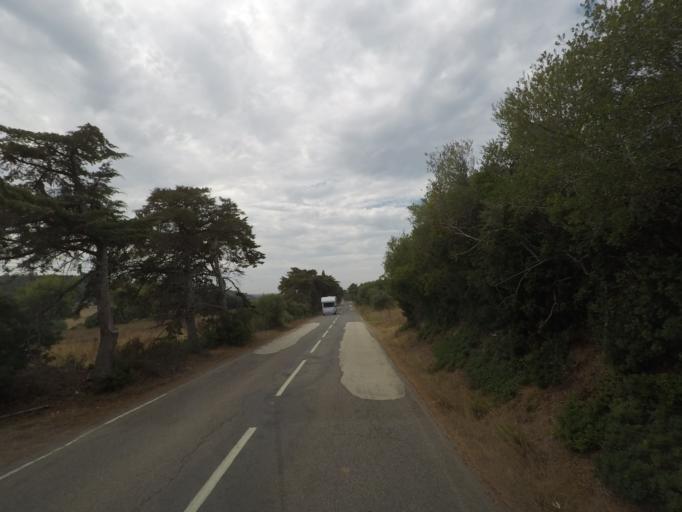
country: PT
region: Faro
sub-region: Aljezur
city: Aljezur
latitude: 37.2569
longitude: -8.8153
